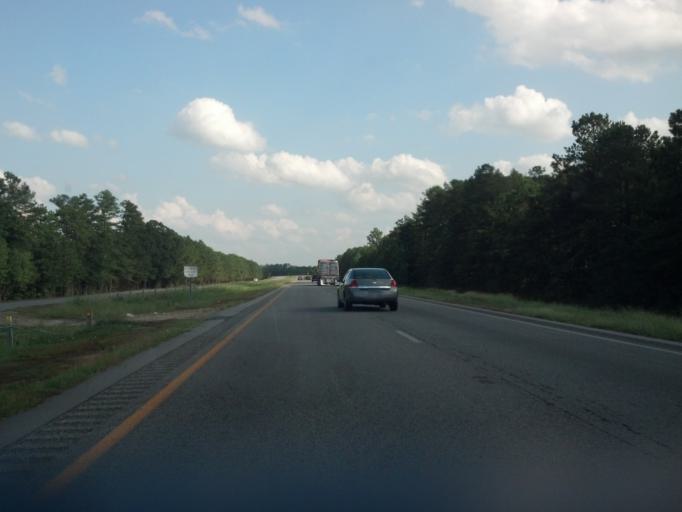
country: US
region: North Carolina
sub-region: Edgecombe County
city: Tarboro
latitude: 35.9058
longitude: -77.6441
